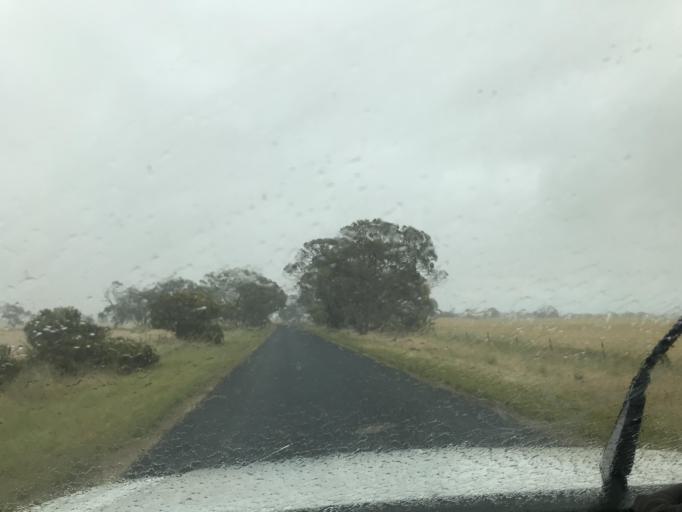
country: AU
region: South Australia
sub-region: Tatiara
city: Bordertown
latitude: -36.3276
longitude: 141.2097
